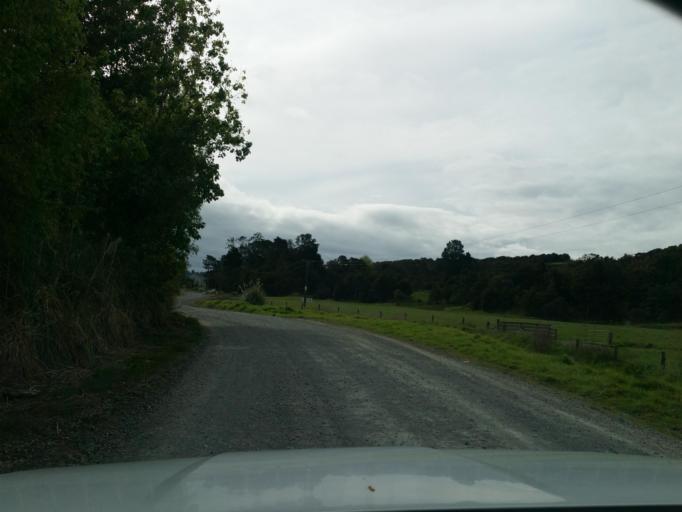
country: NZ
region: Northland
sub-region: Kaipara District
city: Dargaville
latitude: -35.8995
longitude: 173.9192
